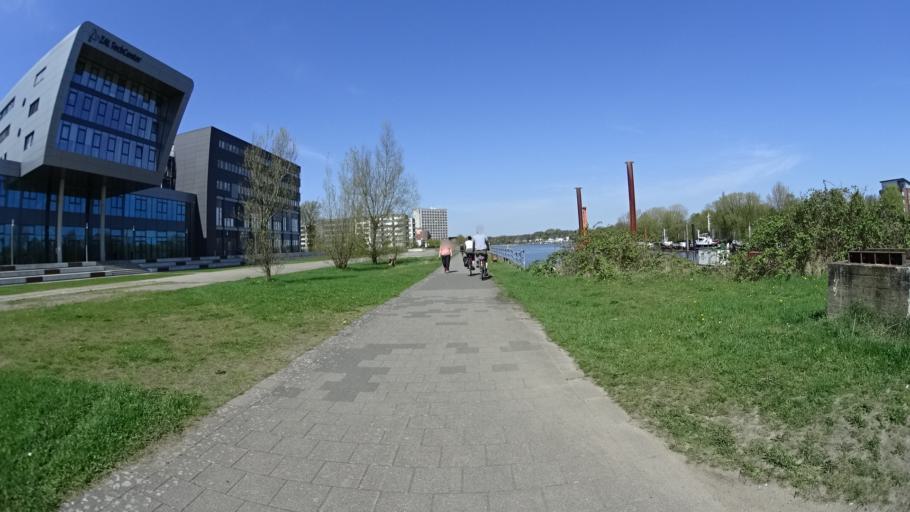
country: DE
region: Hamburg
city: Altona
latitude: 53.5367
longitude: 9.8692
